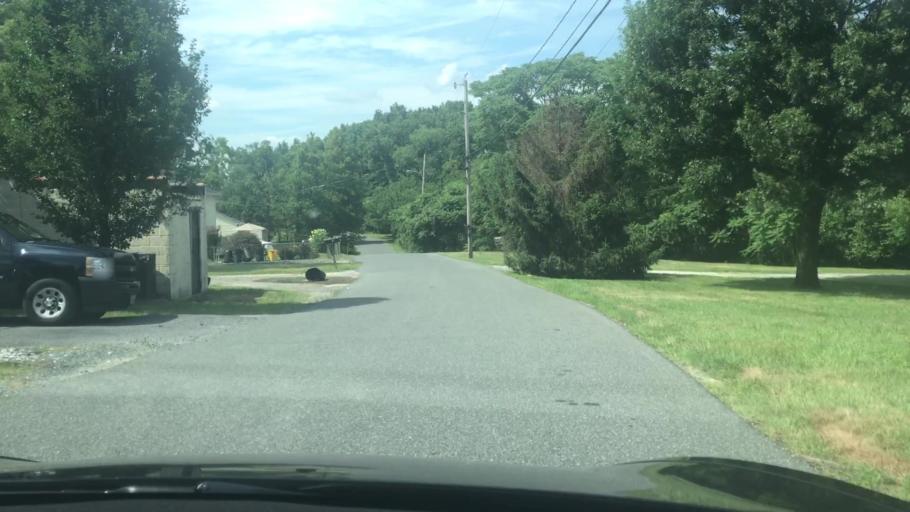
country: US
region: Maryland
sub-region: Baltimore County
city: Edgemere
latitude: 39.2778
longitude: -76.4368
